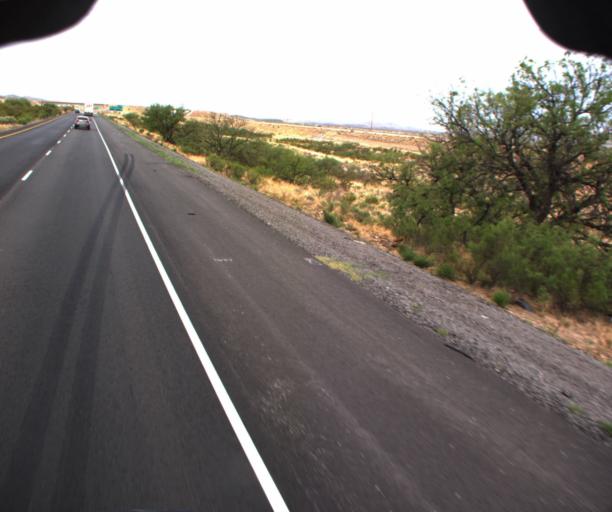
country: US
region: Arizona
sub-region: Cochise County
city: Mescal
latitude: 31.9805
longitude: -110.5273
